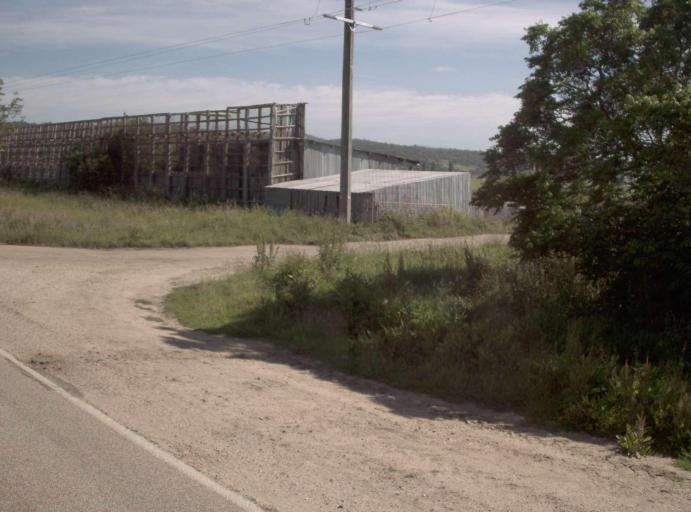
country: AU
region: Victoria
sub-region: East Gippsland
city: Bairnsdale
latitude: -37.7249
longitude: 147.8072
